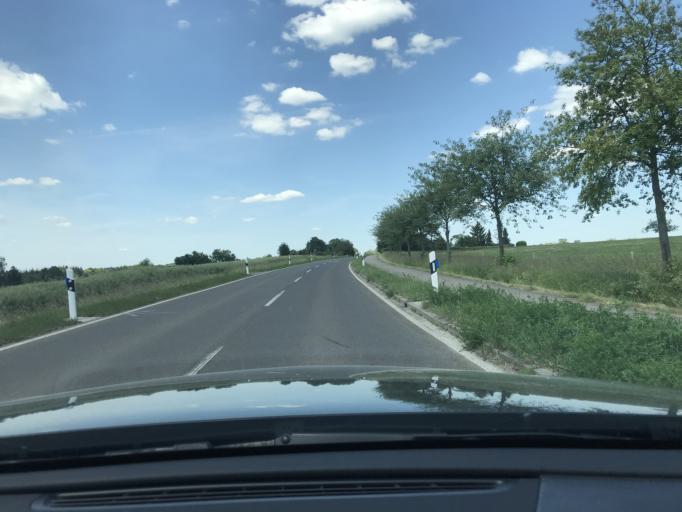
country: DE
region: Baden-Wuerttemberg
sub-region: Regierungsbezirk Stuttgart
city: Altbach
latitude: 48.7646
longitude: 9.3897
